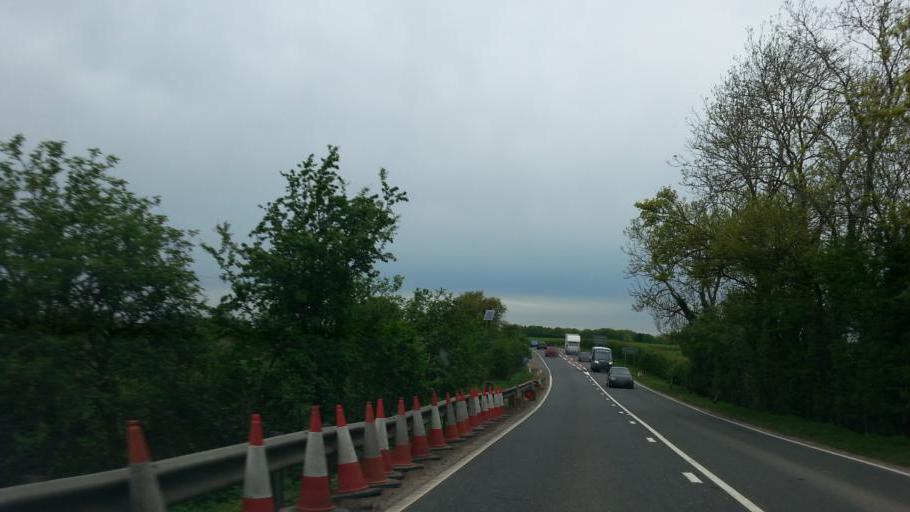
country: GB
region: England
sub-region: Peterborough
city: Wansford
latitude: 52.5834
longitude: -0.3951
